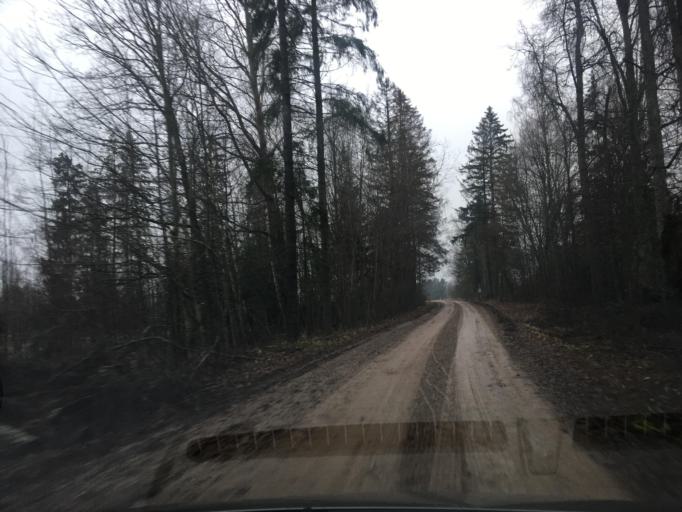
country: EE
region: Tartu
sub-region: Tartu linn
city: Tartu
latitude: 58.3787
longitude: 26.9261
